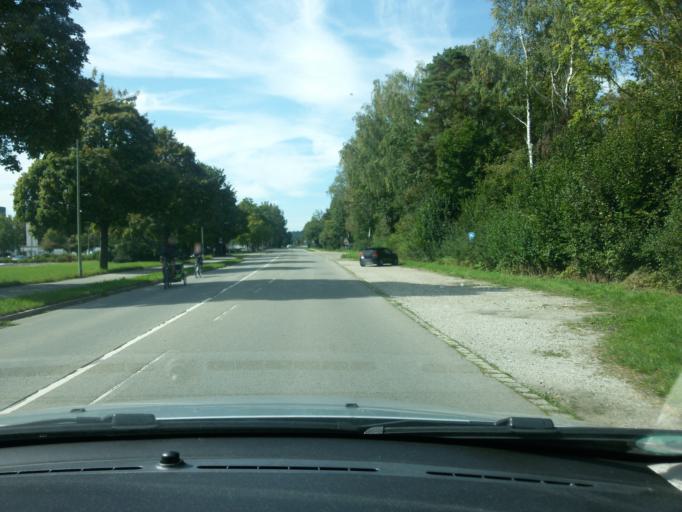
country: DE
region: Bavaria
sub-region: Swabia
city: Bobingen
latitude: 48.2817
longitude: 10.8251
